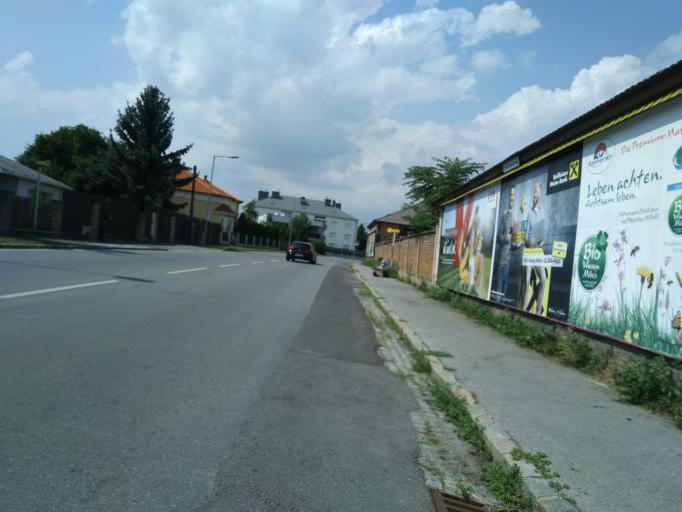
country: AT
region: Lower Austria
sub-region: Politischer Bezirk Ganserndorf
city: Ganserndorf
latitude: 48.3414
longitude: 16.7161
